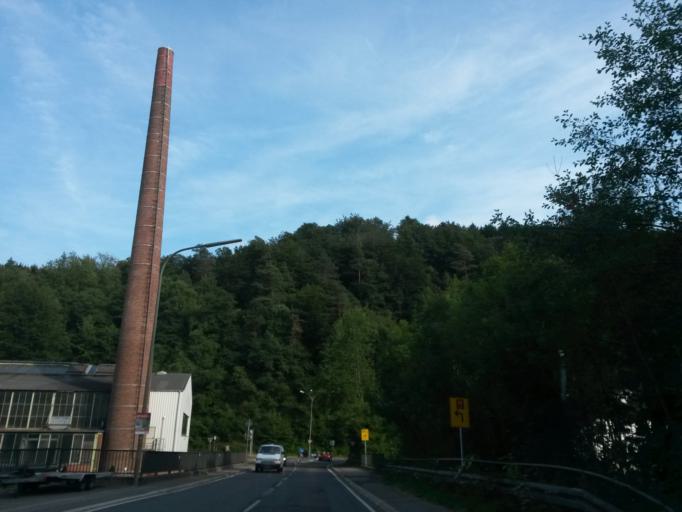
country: DE
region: North Rhine-Westphalia
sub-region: Regierungsbezirk Koln
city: Lindlar
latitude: 51.0342
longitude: 7.4320
